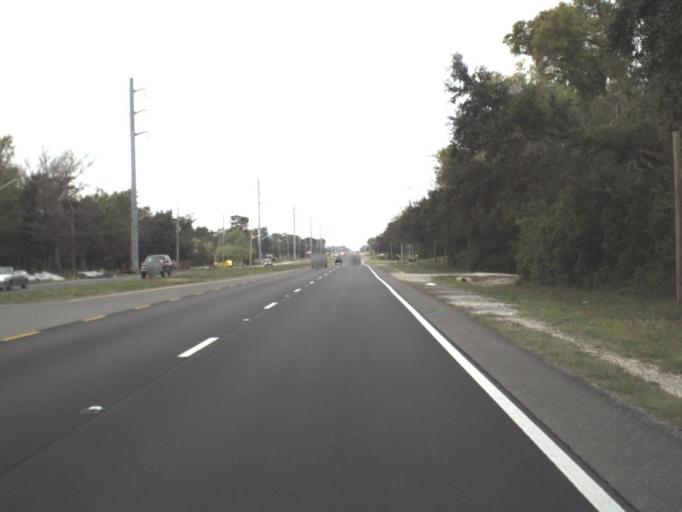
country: US
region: Florida
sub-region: Santa Rosa County
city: Tiger Point
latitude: 30.3959
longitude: -87.0265
